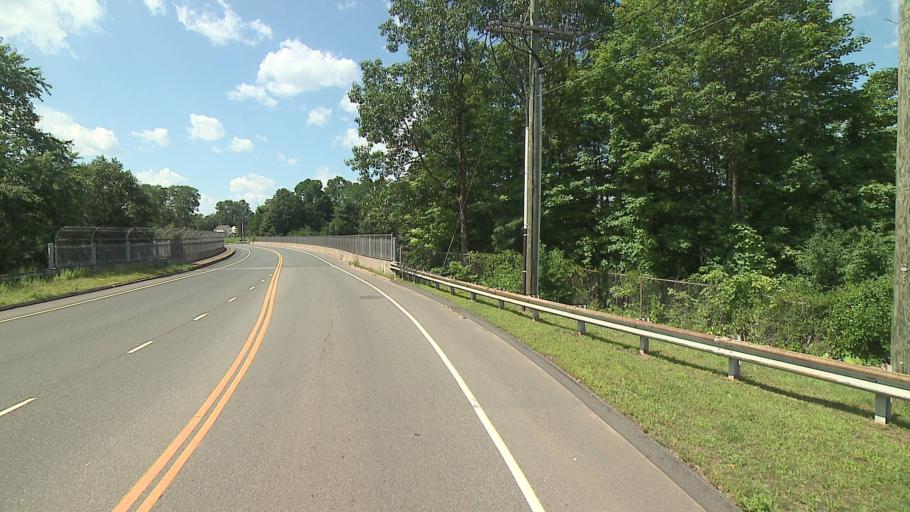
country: US
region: Connecticut
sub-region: Hartford County
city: Farmington
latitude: 41.7226
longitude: -72.7889
